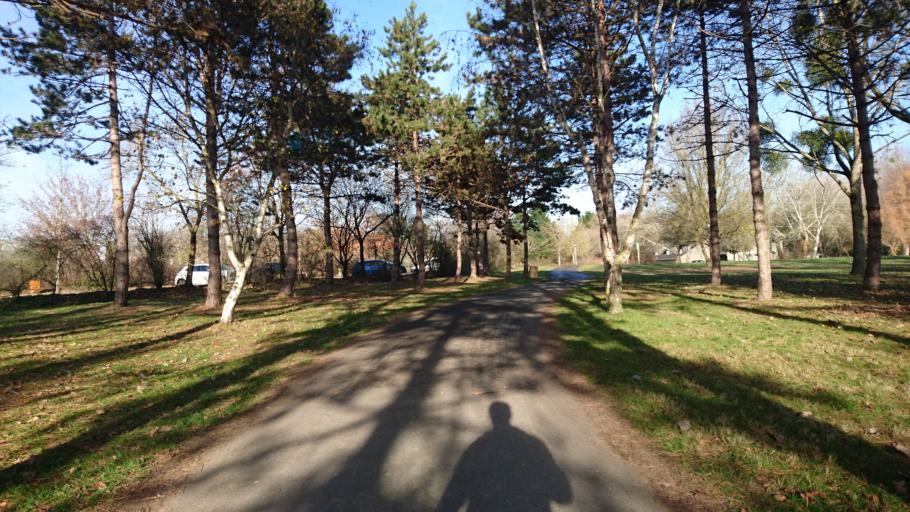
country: FR
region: Pays de la Loire
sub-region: Departement de Maine-et-Loire
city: Avrille
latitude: 47.4650
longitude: -0.5915
